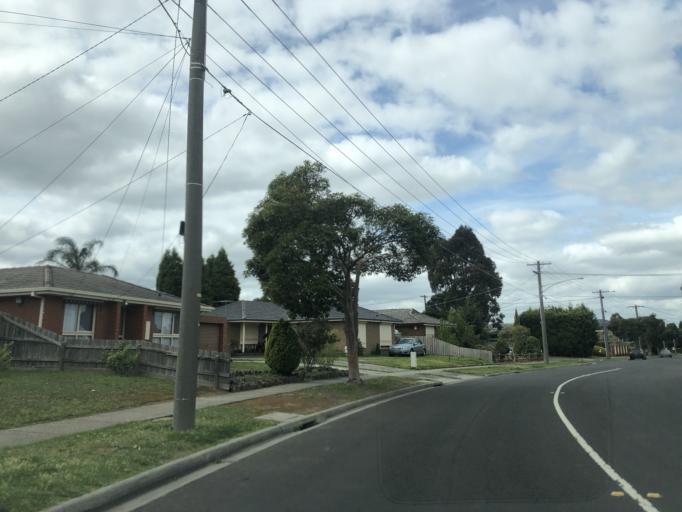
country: AU
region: Victoria
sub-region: Greater Dandenong
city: Dandenong North
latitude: -37.9529
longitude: 145.2091
